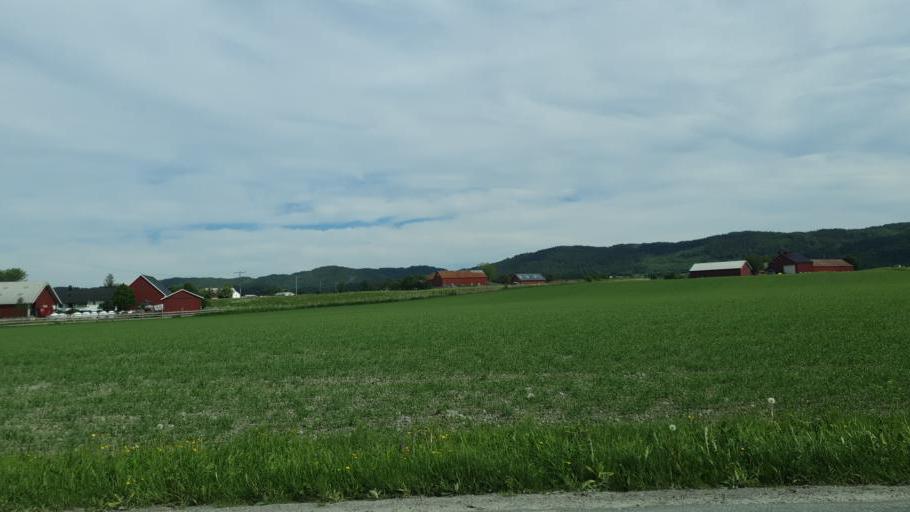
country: NO
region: Sor-Trondelag
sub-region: Rissa
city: Rissa
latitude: 63.5736
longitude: 9.9339
